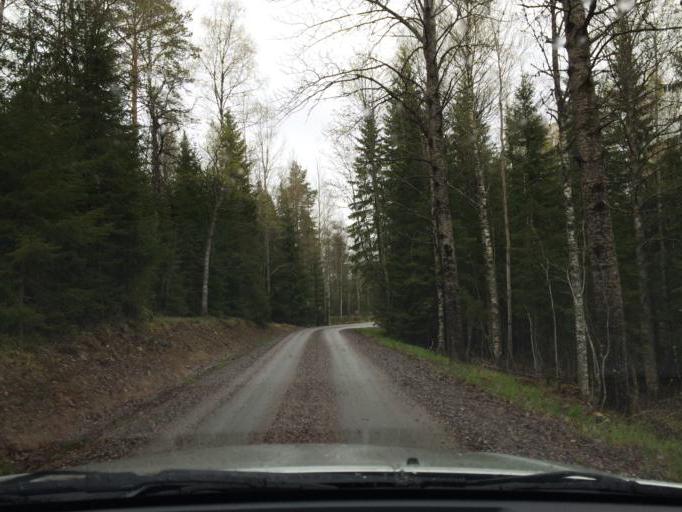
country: SE
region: Dalarna
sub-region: Ludvika Kommun
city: Abborrberget
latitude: 60.0222
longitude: 14.6321
